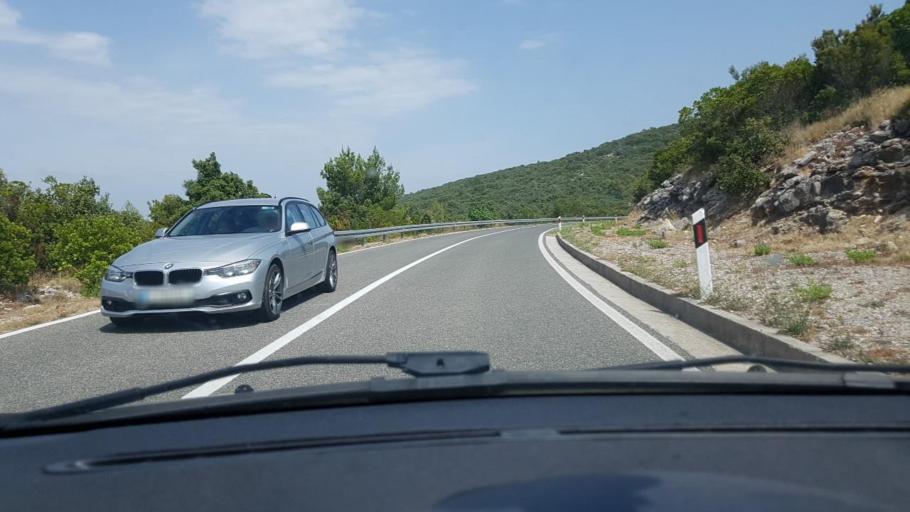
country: HR
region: Dubrovacko-Neretvanska
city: Smokvica
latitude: 42.9493
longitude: 16.9493
